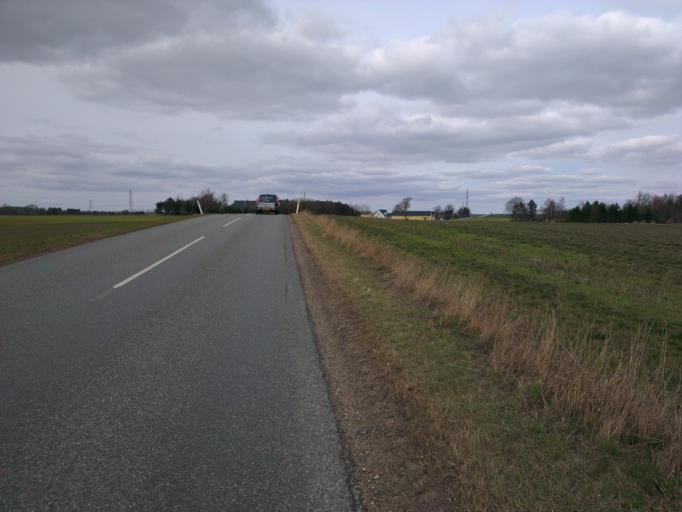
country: DK
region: Capital Region
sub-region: Frederikssund Kommune
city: Skibby
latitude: 55.7900
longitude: 12.0116
